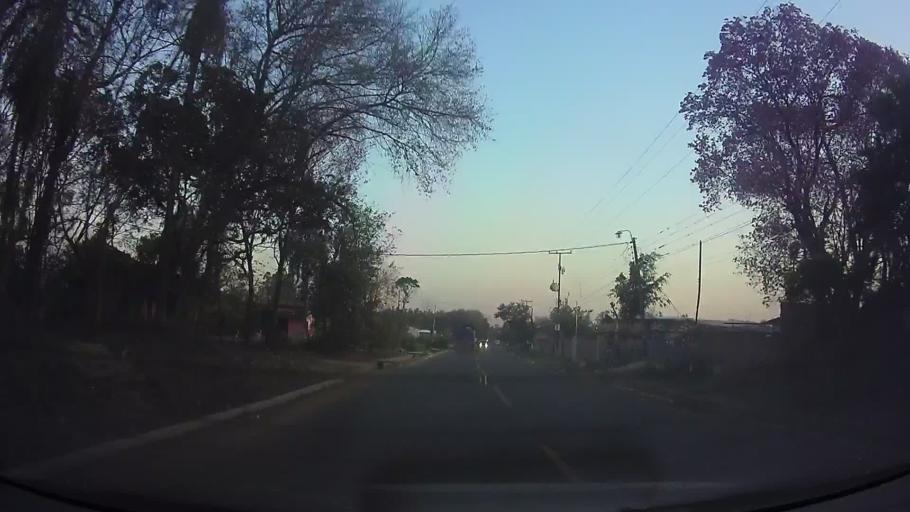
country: PY
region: Central
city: Limpio
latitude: -25.2406
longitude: -57.4909
